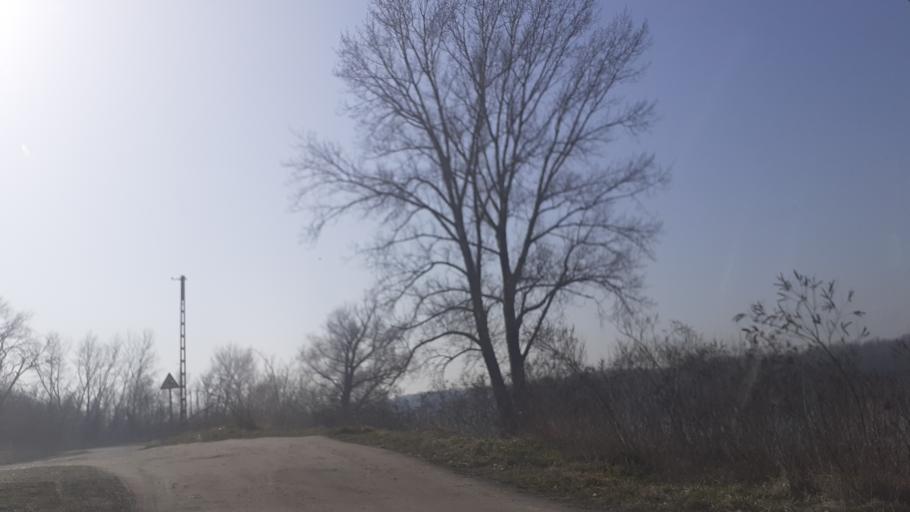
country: HU
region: Fejer
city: Racalmas
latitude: 47.0263
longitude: 18.9722
